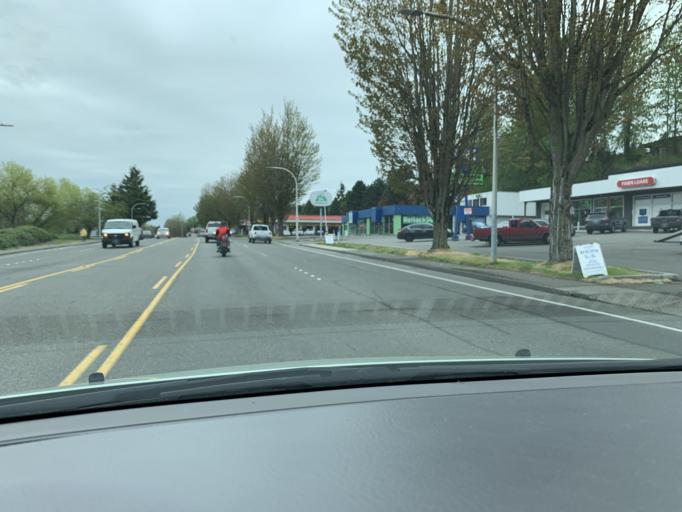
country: US
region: Washington
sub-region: King County
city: Renton
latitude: 47.4893
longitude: -122.2180
